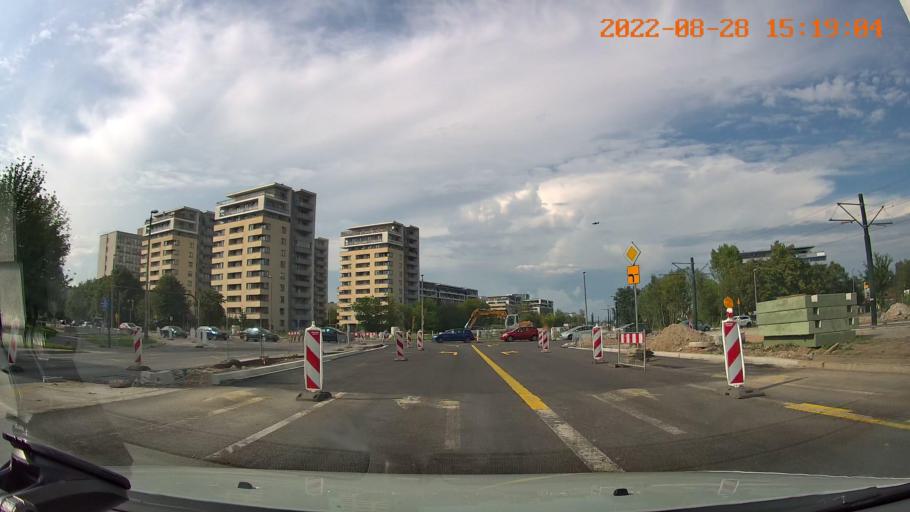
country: PL
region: Lesser Poland Voivodeship
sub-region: Krakow
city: Krakow
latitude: 50.0837
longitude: 19.9344
